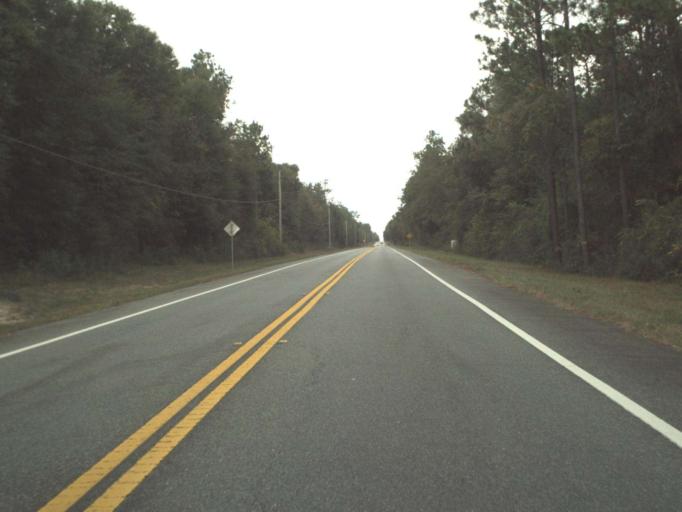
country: US
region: Florida
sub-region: Santa Rosa County
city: Point Baker
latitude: 30.7163
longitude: -87.0454
